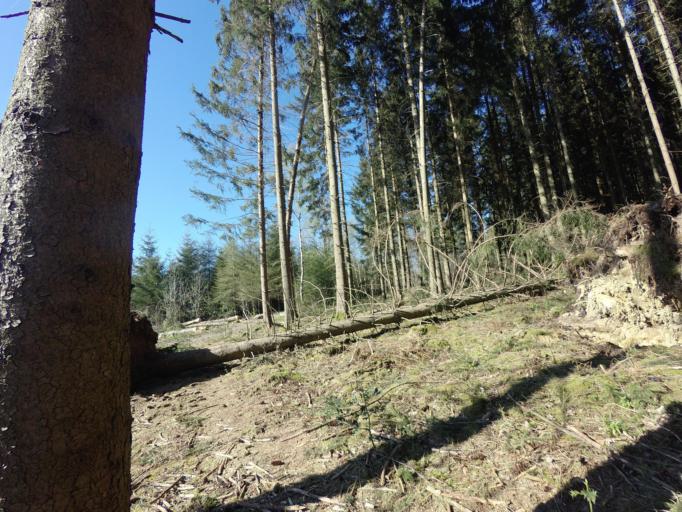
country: BE
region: Wallonia
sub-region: Province de Liege
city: Trois-Ponts
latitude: 50.3968
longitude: 5.8874
